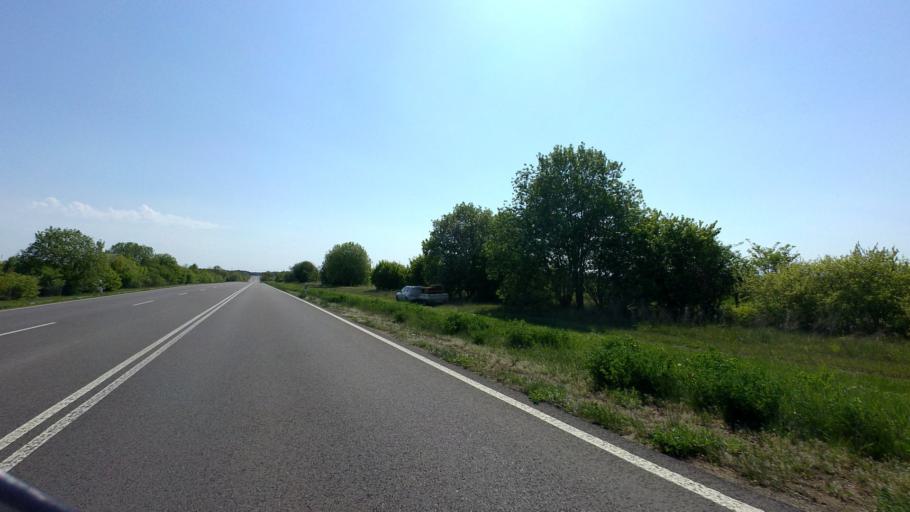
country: DE
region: Brandenburg
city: Beeskow
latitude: 52.1761
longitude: 14.2167
